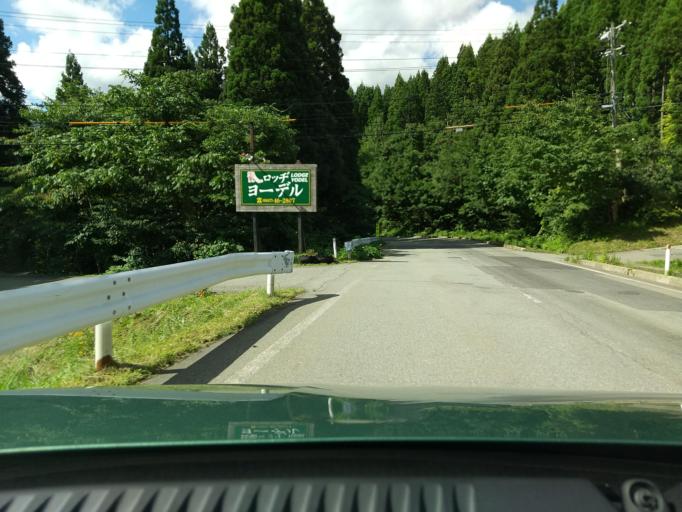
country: JP
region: Iwate
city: Shizukuishi
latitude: 39.7657
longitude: 140.7560
